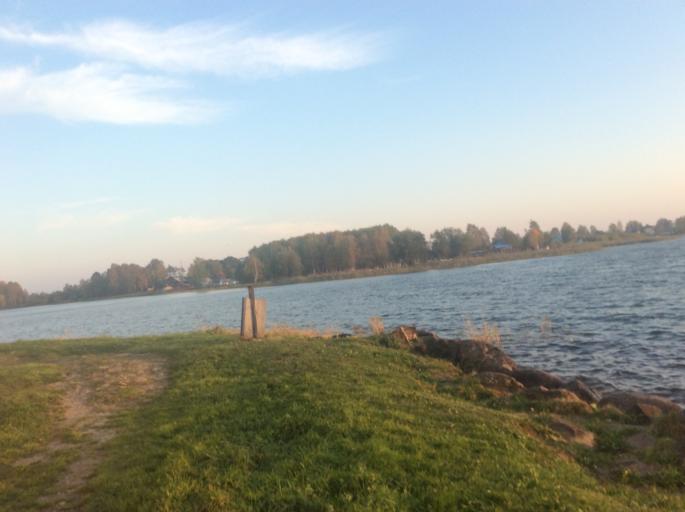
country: RU
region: Vologda
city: Kirillov
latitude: 59.8561
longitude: 38.3667
